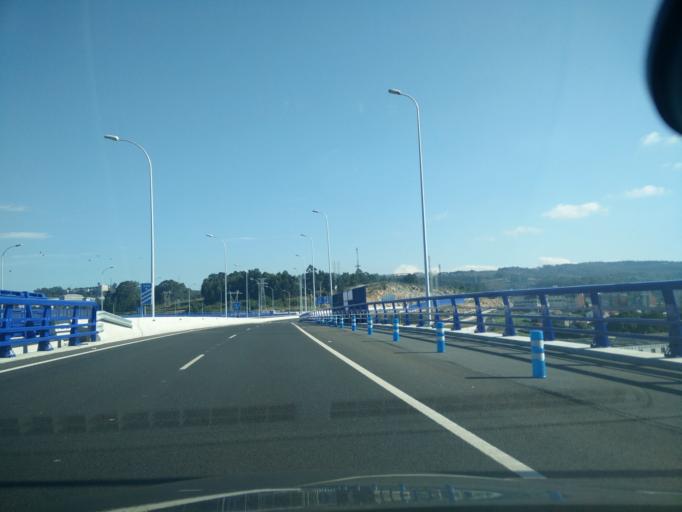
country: ES
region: Galicia
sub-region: Provincia da Coruna
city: A Coruna
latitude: 43.3375
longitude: -8.4227
